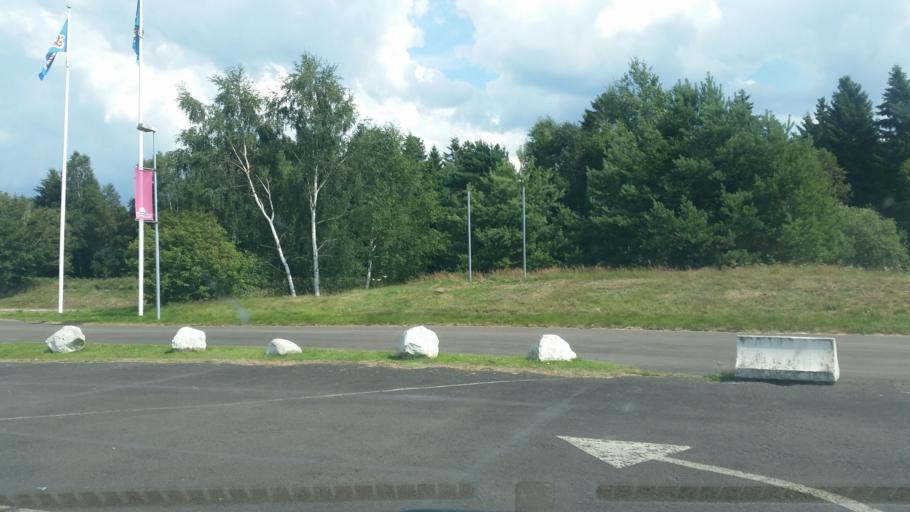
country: SE
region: Vaestra Goetaland
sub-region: Skara Kommun
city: Axvall
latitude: 58.4032
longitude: 13.5504
